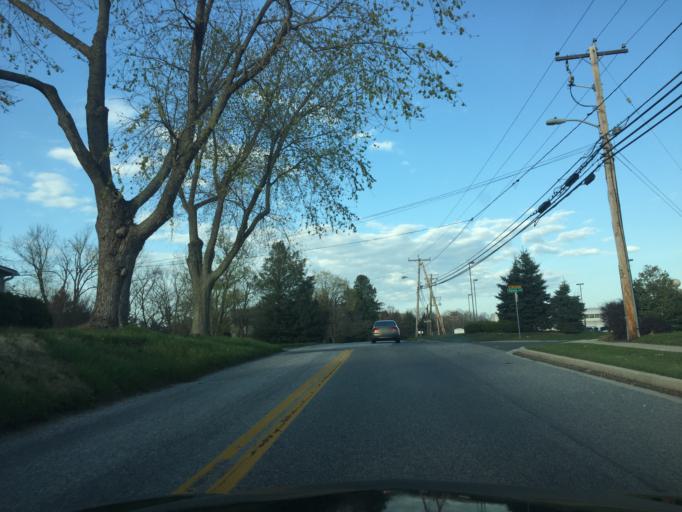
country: US
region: Maryland
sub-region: Baltimore County
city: Perry Hall
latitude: 39.4019
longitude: -76.4506
